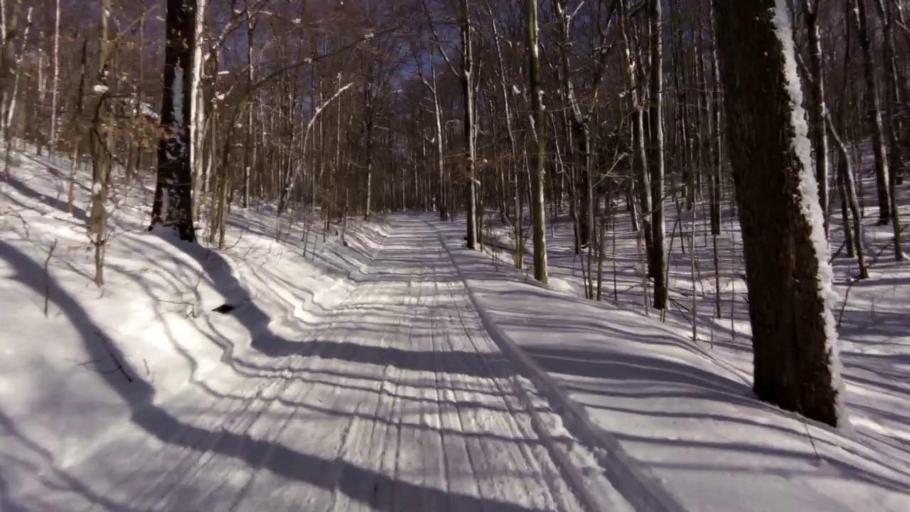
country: US
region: New York
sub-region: Cattaraugus County
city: Salamanca
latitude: 42.0652
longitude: -78.6689
